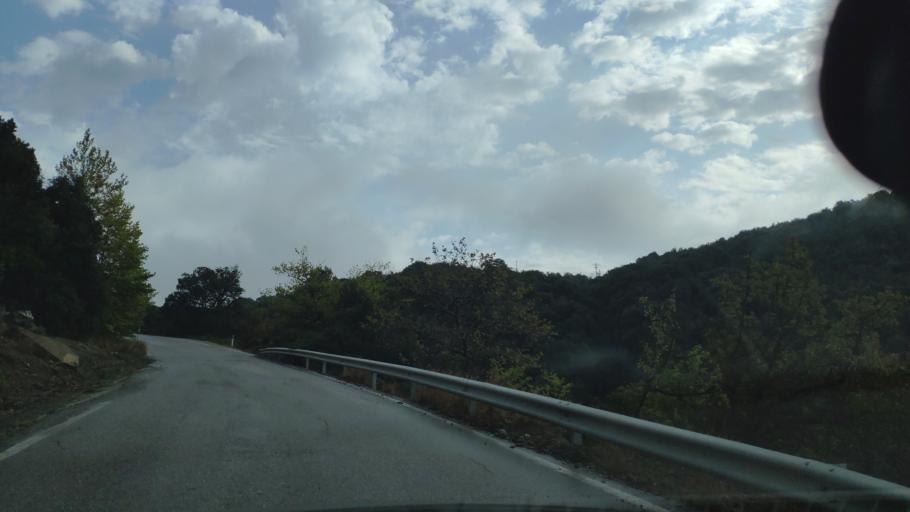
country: GR
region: West Greece
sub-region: Nomos Aitolias kai Akarnanias
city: Sardinia
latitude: 38.8762
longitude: 21.2615
